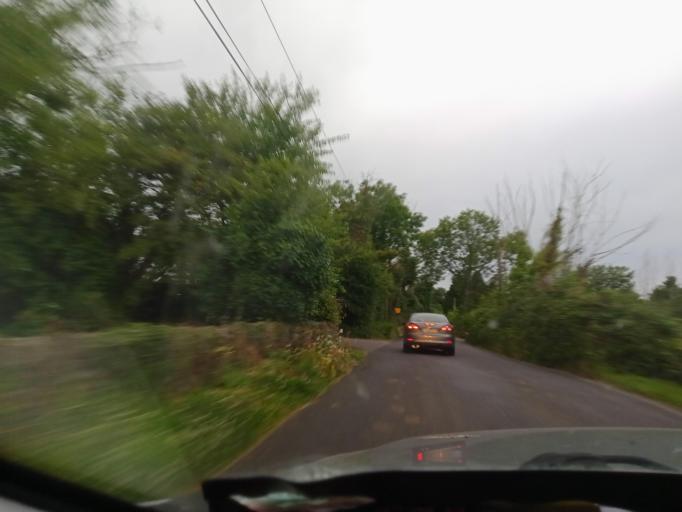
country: IE
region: Leinster
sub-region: Laois
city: Mountmellick
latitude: 53.1114
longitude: -7.3548
